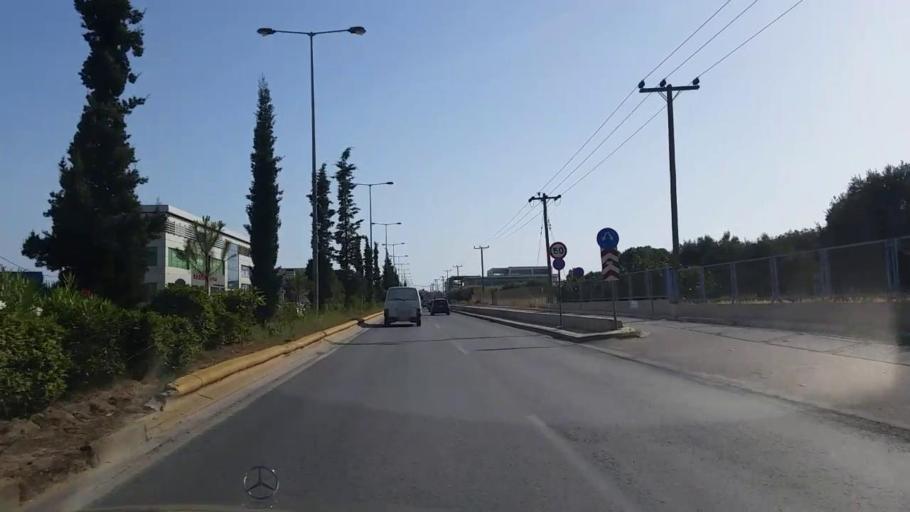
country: GR
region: Attica
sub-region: Nomarchia Anatolikis Attikis
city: Koropi
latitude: 37.8856
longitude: 23.8782
